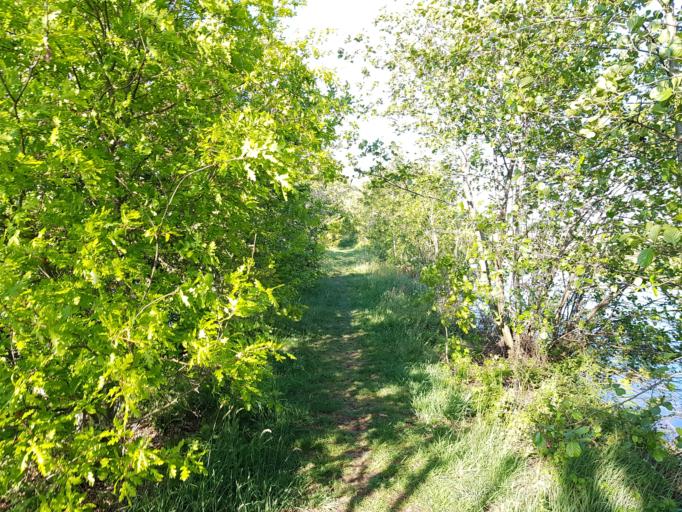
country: NL
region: Utrecht
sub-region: Gemeente Lopik
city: Lopik
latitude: 51.9871
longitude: 4.9171
